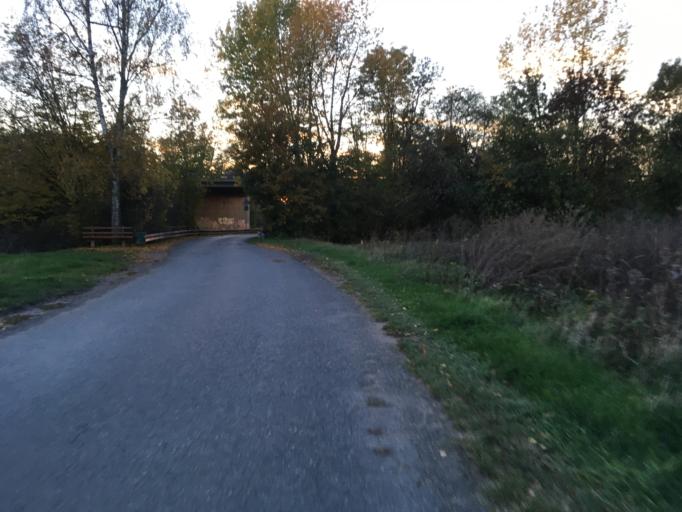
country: DE
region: Hesse
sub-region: Regierungsbezirk Darmstadt
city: Bensheim
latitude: 49.6683
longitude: 8.6033
